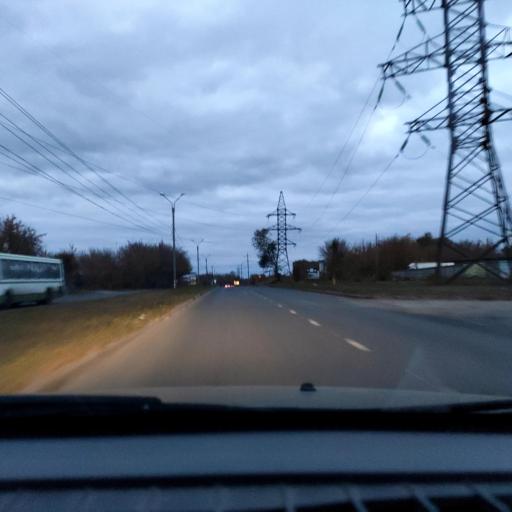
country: RU
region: Samara
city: Tol'yatti
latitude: 53.5530
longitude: 49.3185
